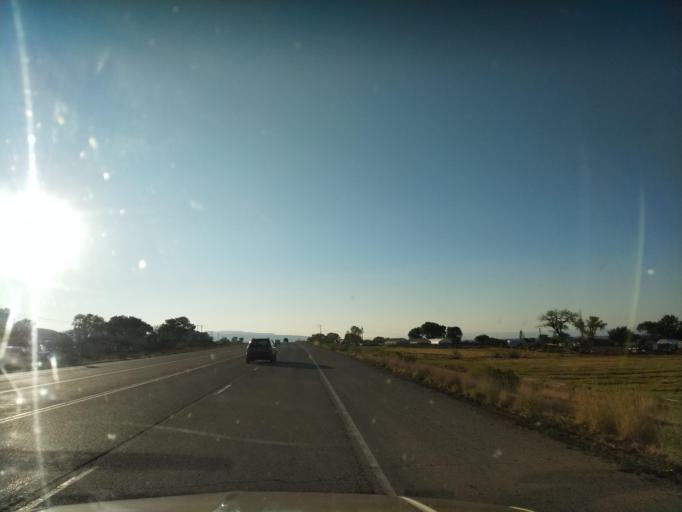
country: US
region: Colorado
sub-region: Mesa County
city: Fruitvale
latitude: 39.0213
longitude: -108.4884
